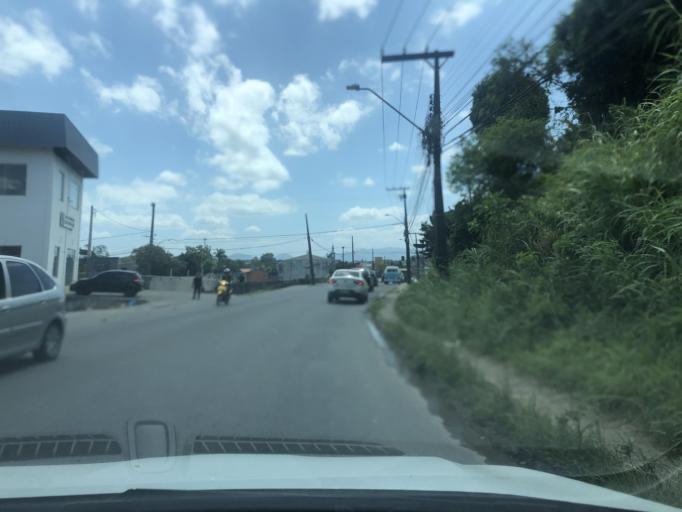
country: BR
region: Santa Catarina
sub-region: Joinville
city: Joinville
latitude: -26.3395
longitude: -48.8074
